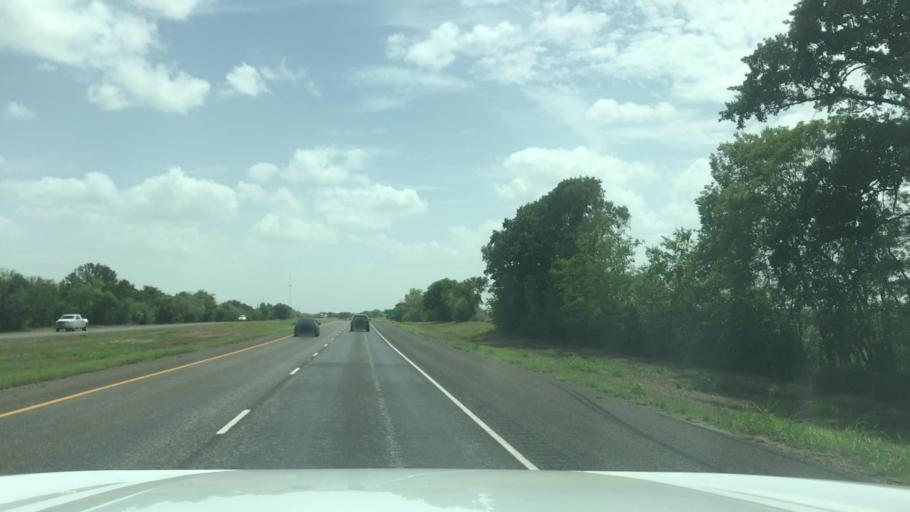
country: US
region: Texas
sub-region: Falls County
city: Marlin
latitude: 31.2899
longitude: -96.8752
